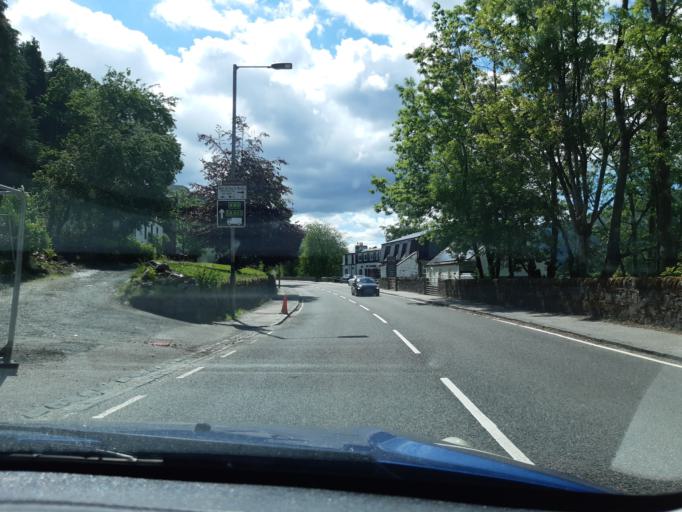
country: GB
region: Scotland
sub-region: Argyll and Bute
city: Garelochhead
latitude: 56.2028
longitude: -4.7439
